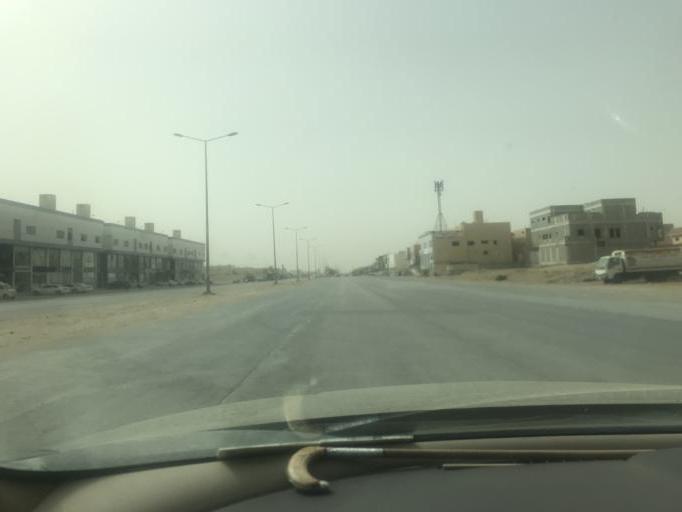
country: SA
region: Ar Riyad
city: Riyadh
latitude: 24.8063
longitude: 46.6025
